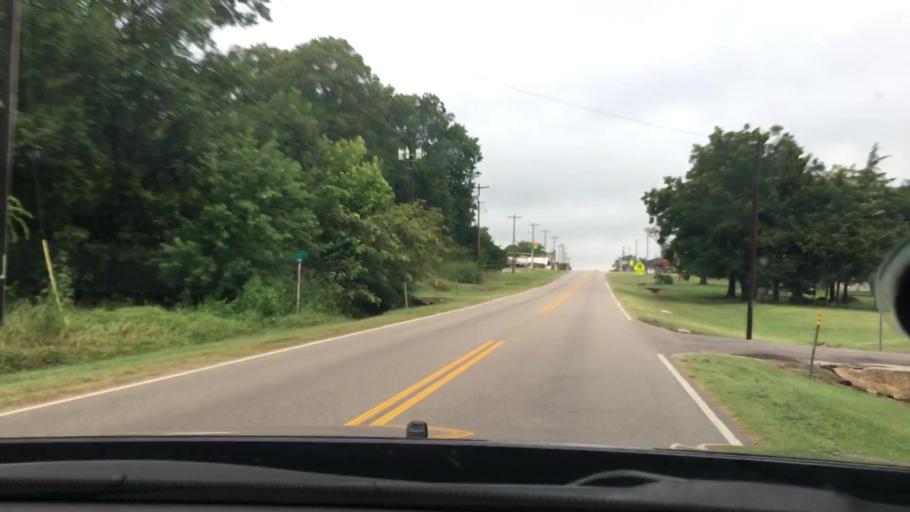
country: US
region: Oklahoma
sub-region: Murray County
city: Sulphur
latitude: 34.6274
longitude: -96.8381
